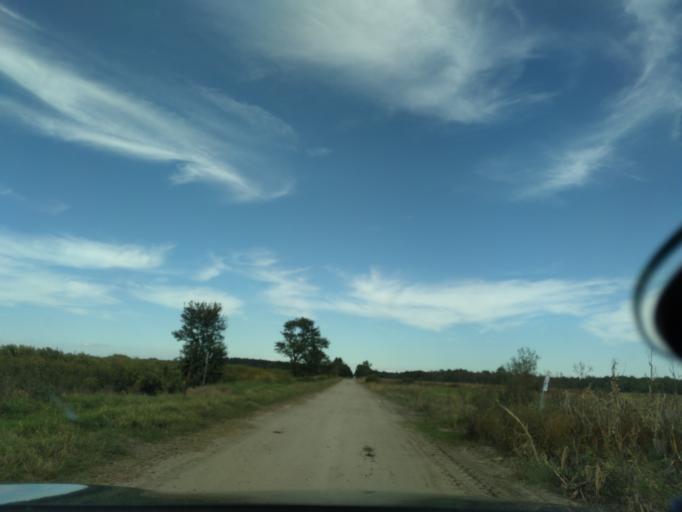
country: US
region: North Carolina
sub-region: Beaufort County
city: Belhaven
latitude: 35.7085
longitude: -76.5858
